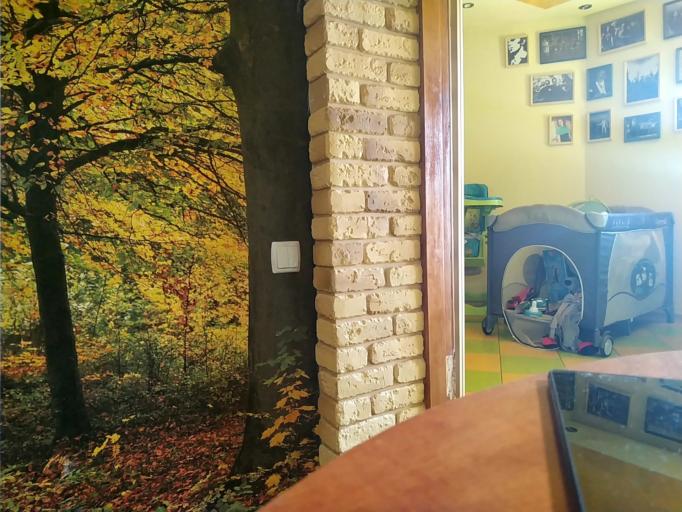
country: RU
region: Tverskaya
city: Vyshniy Volochek
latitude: 57.5891
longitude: 34.5558
